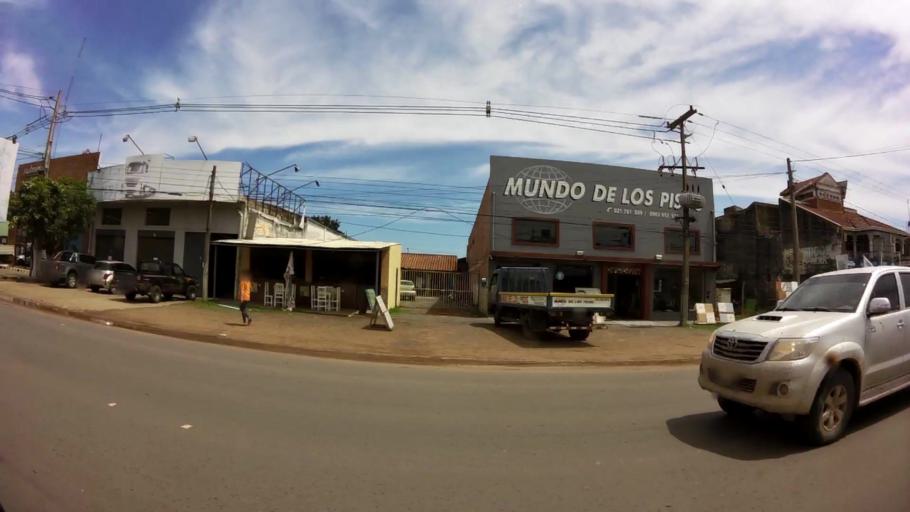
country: PY
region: Central
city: Colonia Mariano Roque Alonso
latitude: -25.2058
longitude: -57.5266
